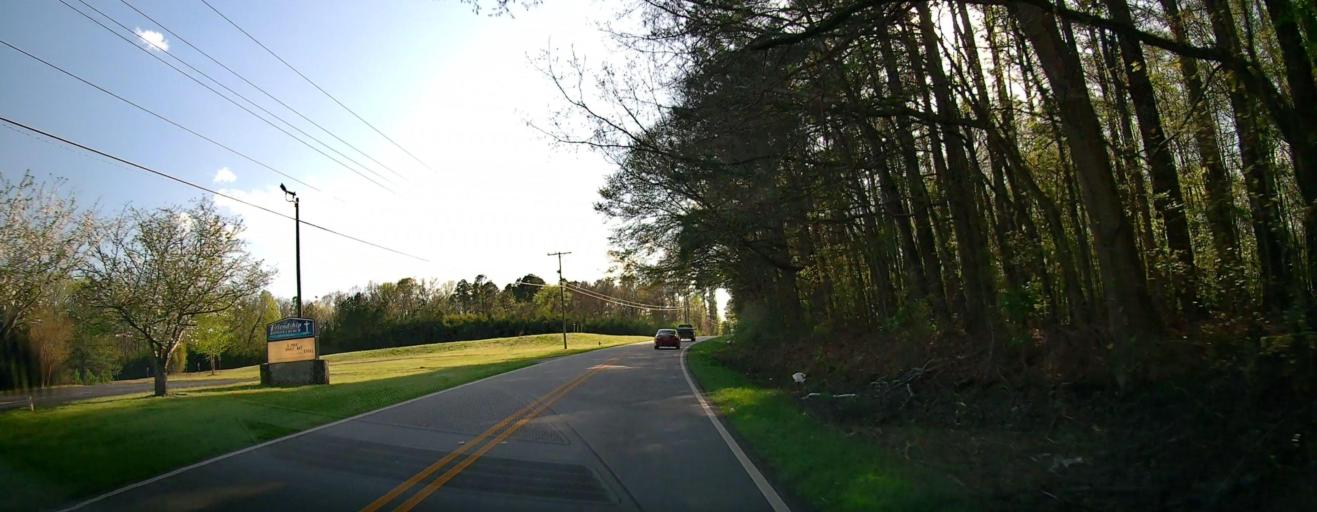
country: US
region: Georgia
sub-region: Putnam County
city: Eatonton
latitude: 33.1996
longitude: -83.3847
